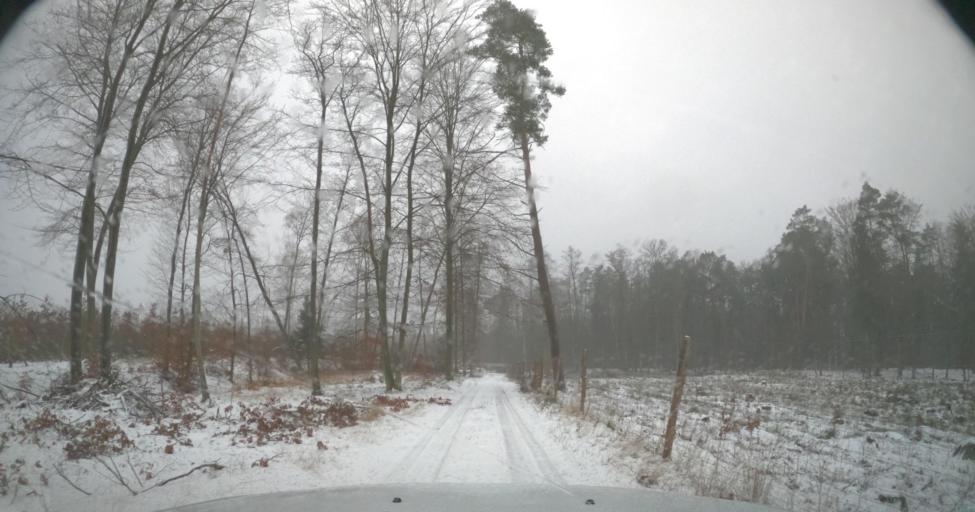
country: PL
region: West Pomeranian Voivodeship
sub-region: Powiat goleniowski
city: Przybiernow
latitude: 53.7099
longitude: 14.8805
